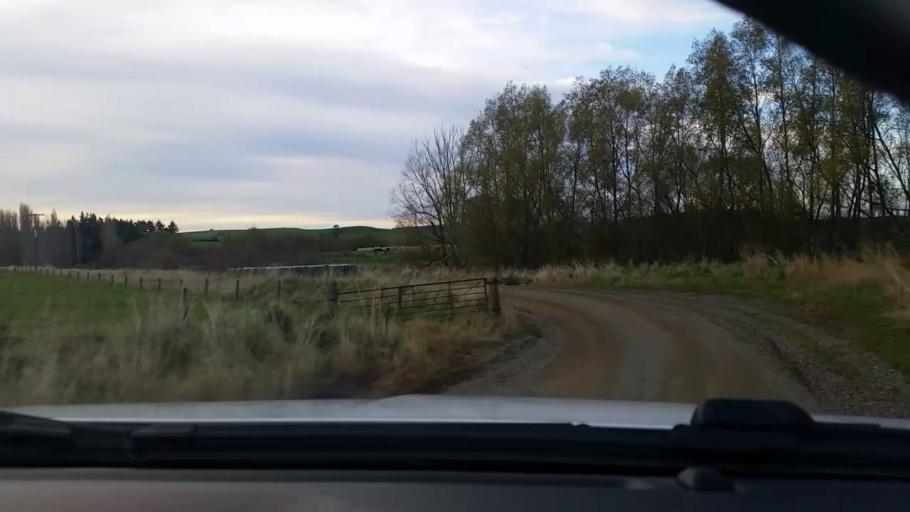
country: NZ
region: Southland
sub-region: Southland District
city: Winton
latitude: -46.1040
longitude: 168.4900
